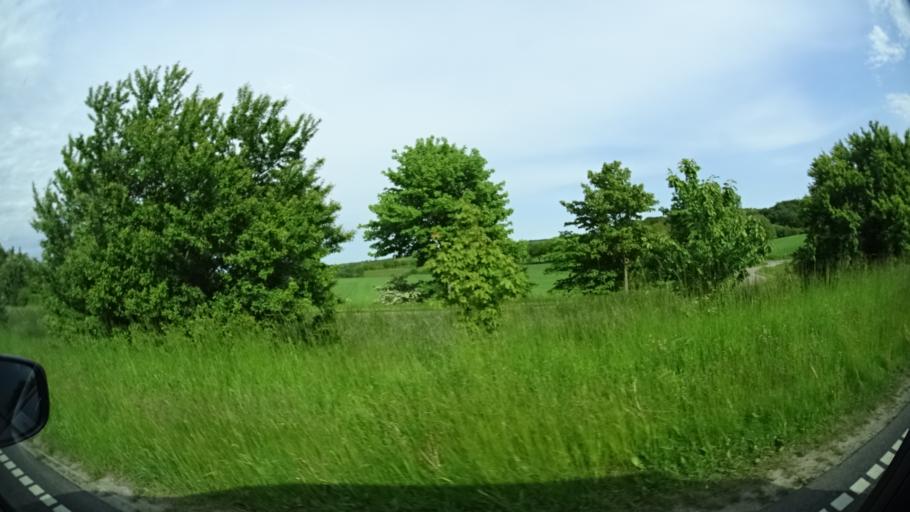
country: DK
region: Central Jutland
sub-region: Arhus Kommune
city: Beder
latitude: 56.0755
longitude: 10.2082
